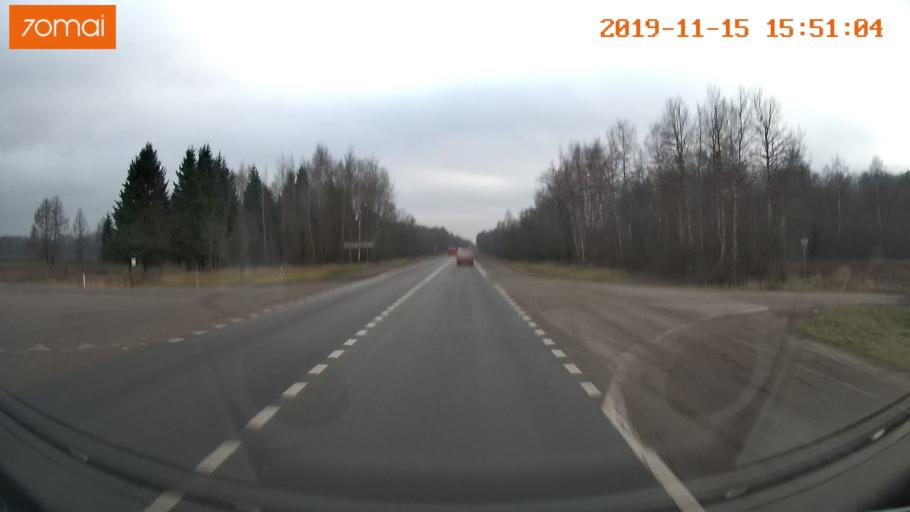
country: RU
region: Jaroslavl
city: Yaroslavl
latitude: 57.8989
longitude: 40.0103
